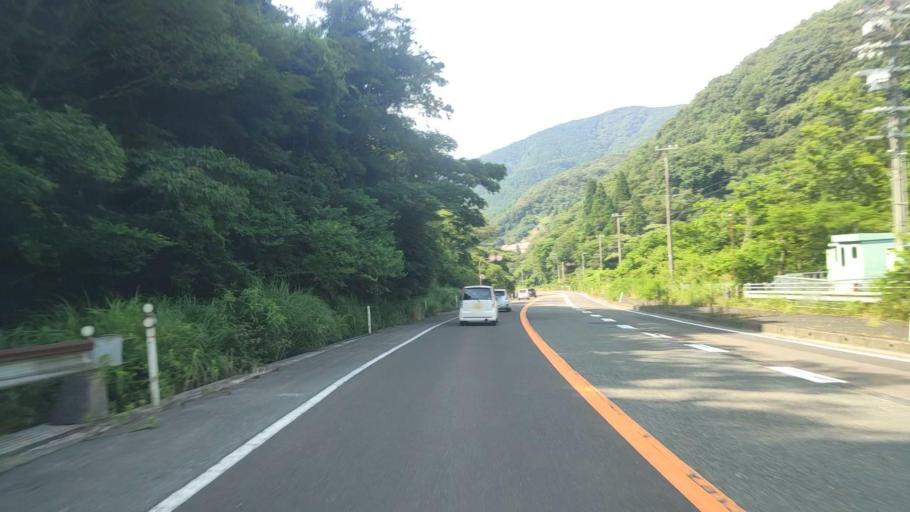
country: JP
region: Fukui
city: Tsuruga
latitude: 35.6012
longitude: 136.1220
